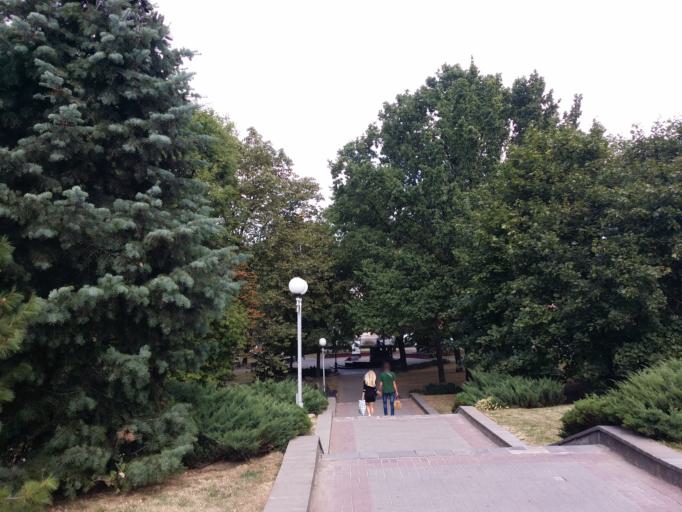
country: BY
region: Minsk
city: Minsk
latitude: 53.9000
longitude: 27.5495
